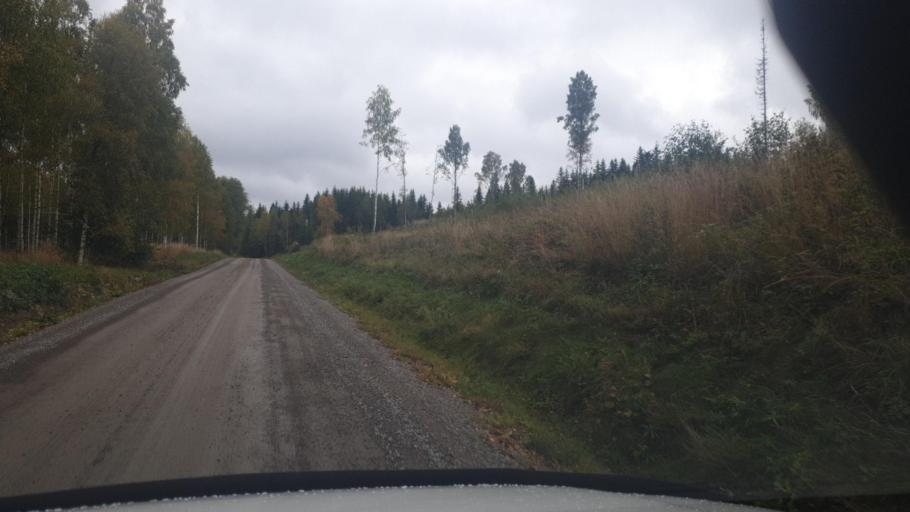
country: SE
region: Vaermland
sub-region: Arvika Kommun
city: Arvika
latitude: 59.9425
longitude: 12.6606
